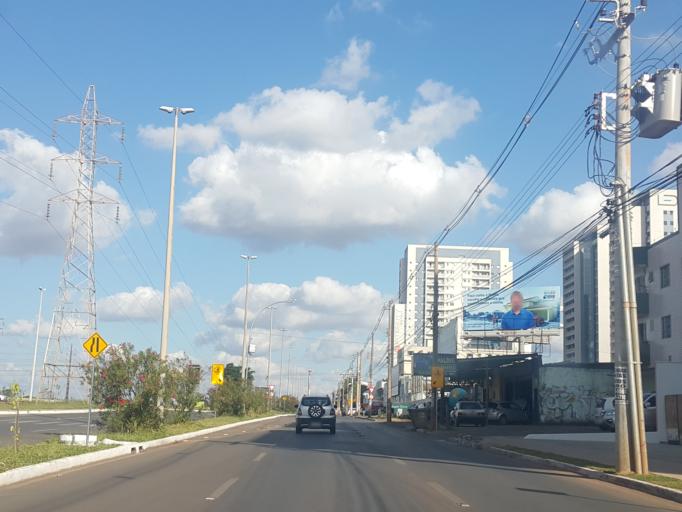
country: BR
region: Federal District
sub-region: Brasilia
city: Brasilia
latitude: -15.8364
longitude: -48.0450
